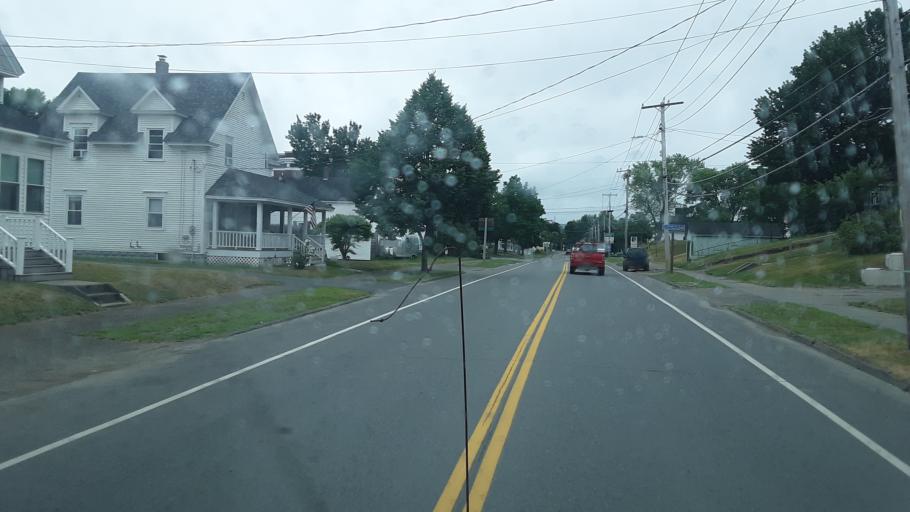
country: US
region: Maine
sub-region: Penobscot County
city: Millinocket
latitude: 45.6601
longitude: -68.7128
